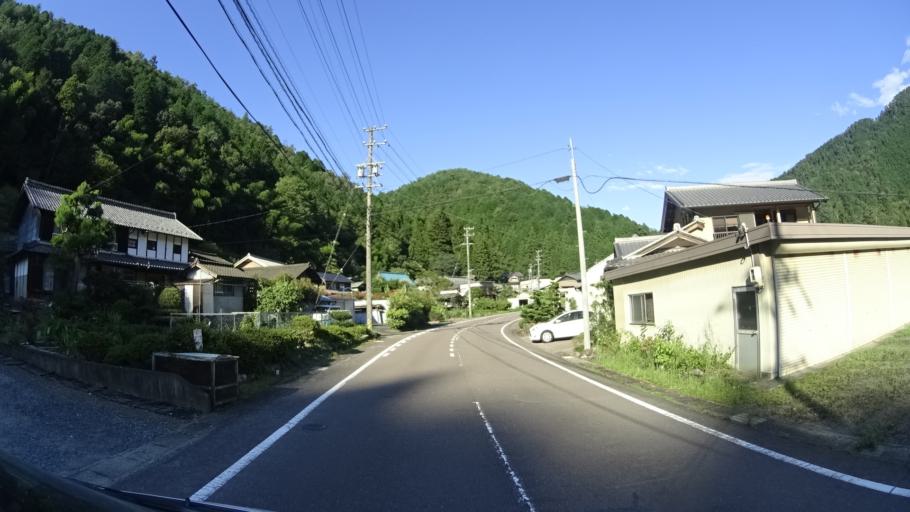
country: JP
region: Gifu
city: Minokamo
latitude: 35.5640
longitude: 137.0946
